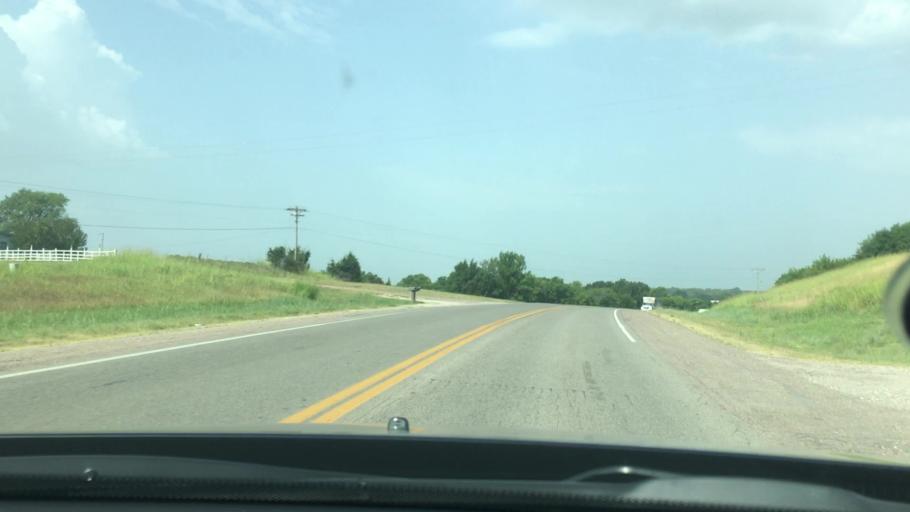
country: US
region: Oklahoma
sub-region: Pontotoc County
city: Ada
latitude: 34.7825
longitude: -96.7436
